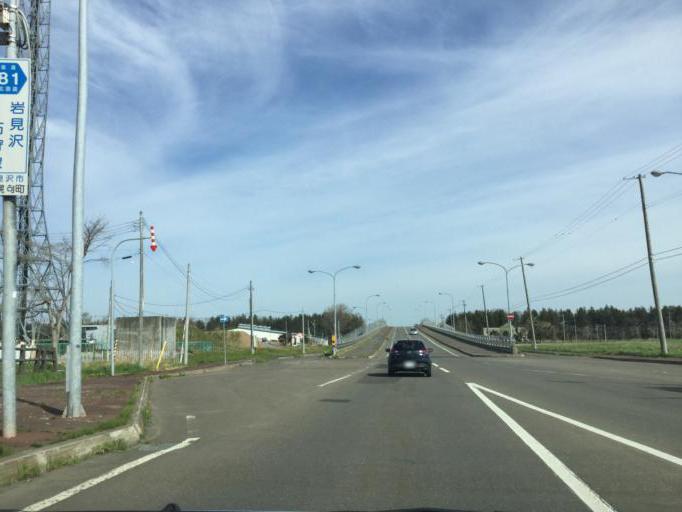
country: JP
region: Hokkaido
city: Iwamizawa
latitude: 43.1751
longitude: 141.7096
